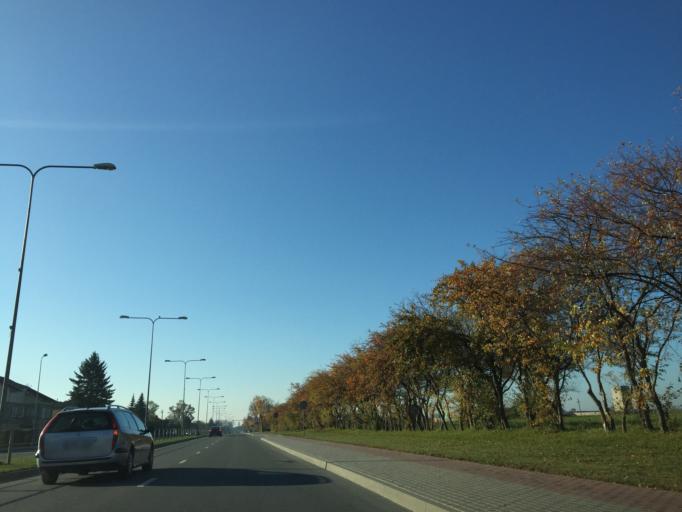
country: LT
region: Klaipedos apskritis
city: Kretinga
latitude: 55.8950
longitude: 21.2359
